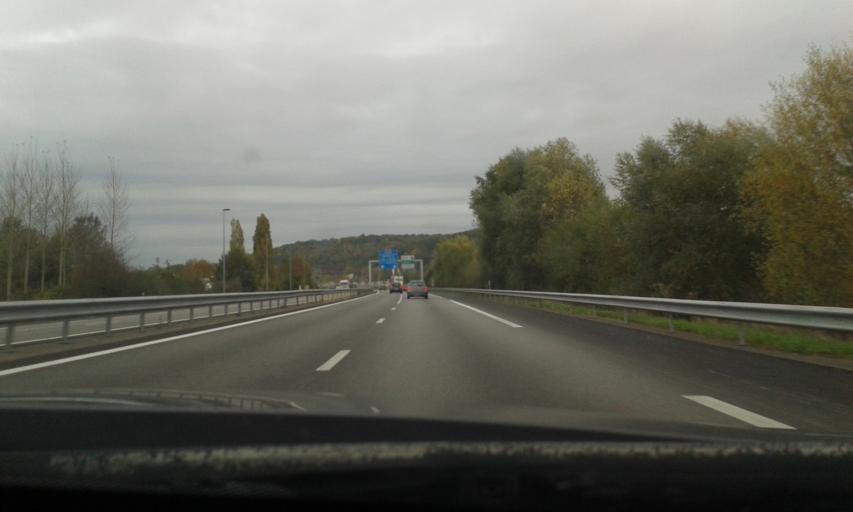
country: FR
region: Haute-Normandie
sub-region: Departement de l'Eure
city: Louviers
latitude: 49.2031
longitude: 1.1786
